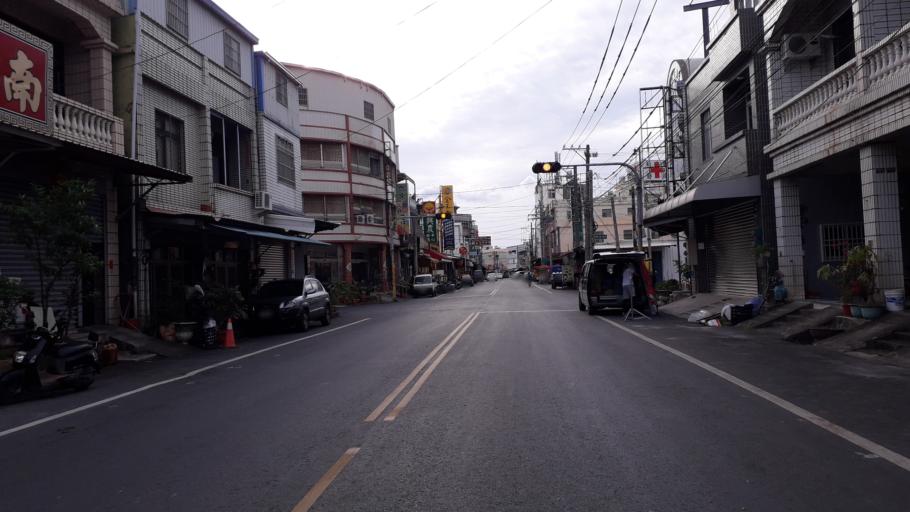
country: TW
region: Taiwan
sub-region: Pingtung
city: Pingtung
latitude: 22.3644
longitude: 120.5987
